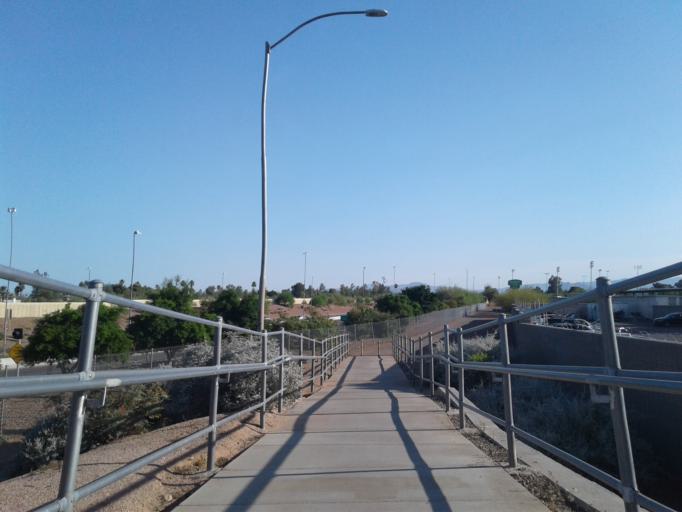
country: US
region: Arizona
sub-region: Maricopa County
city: Paradise Valley
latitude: 33.6412
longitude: -112.0018
